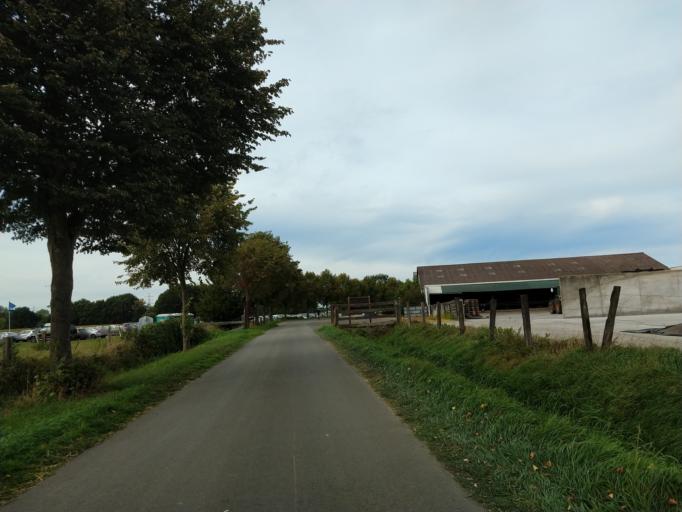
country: BE
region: Flanders
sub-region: Provincie Vlaams-Brabant
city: Haacht
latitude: 50.9696
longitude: 4.6675
